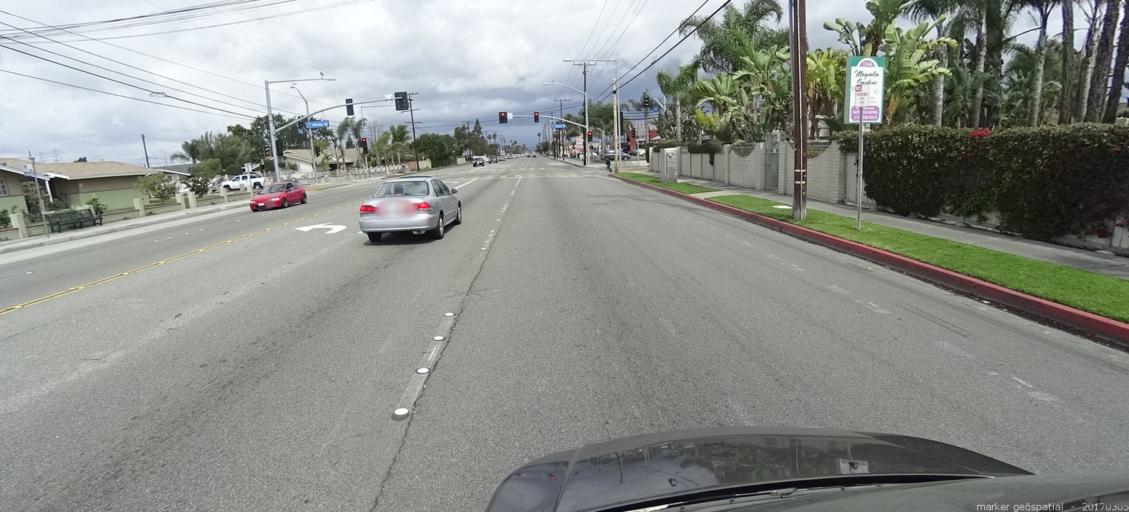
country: US
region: California
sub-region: Orange County
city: Stanton
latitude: 33.8134
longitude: -117.9757
